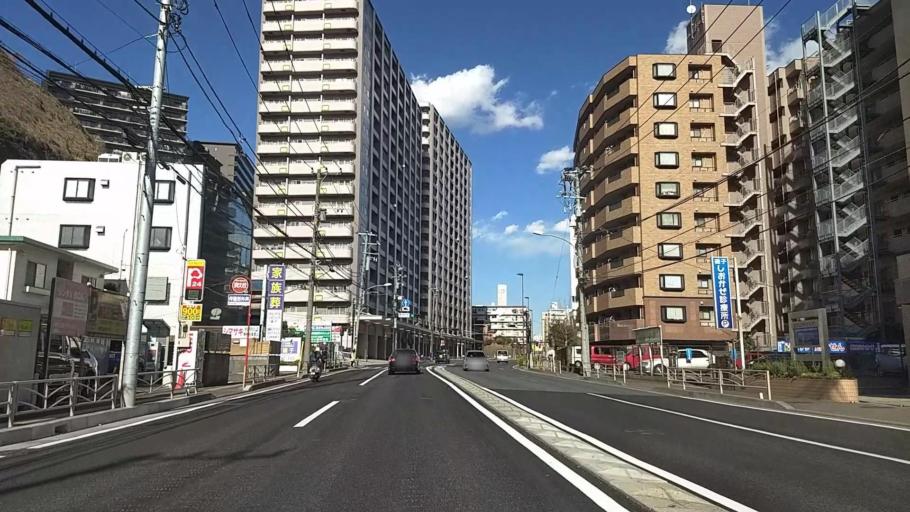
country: JP
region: Kanagawa
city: Yokohama
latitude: 35.4005
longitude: 139.6161
